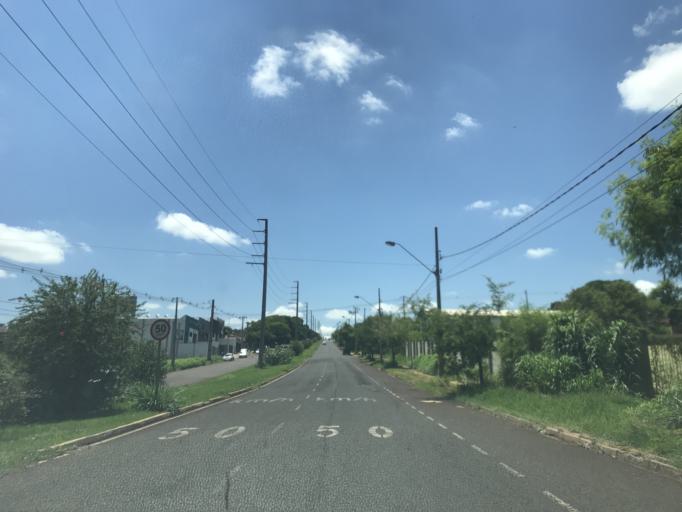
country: BR
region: Parana
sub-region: Maringa
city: Maringa
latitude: -23.4548
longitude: -51.9305
